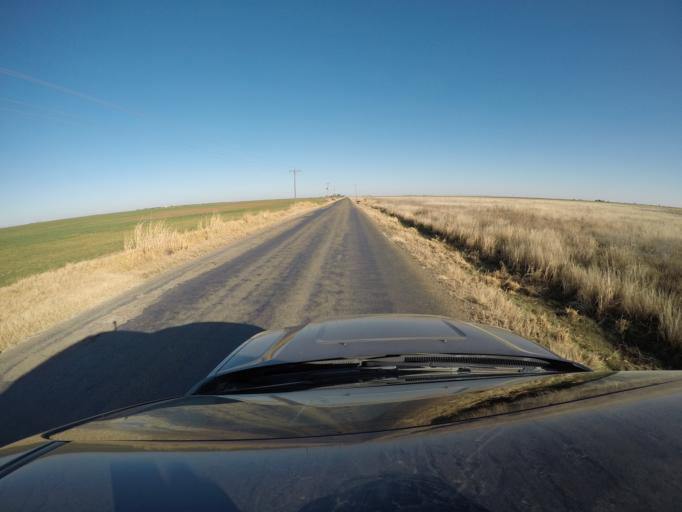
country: US
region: Texas
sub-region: Parmer County
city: Farwell
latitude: 34.3026
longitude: -103.0710
